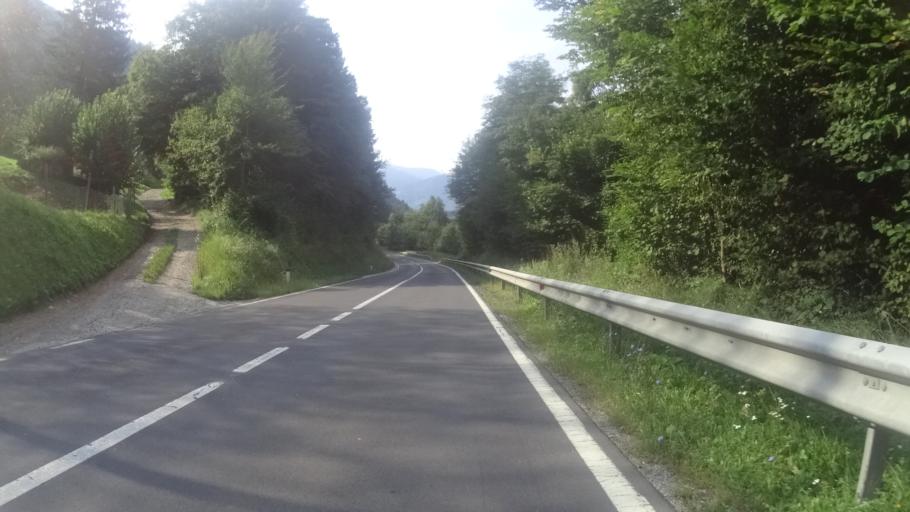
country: SI
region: Selnica ob Dravi
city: Selnica ob Dravi
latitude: 46.5705
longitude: 15.4576
